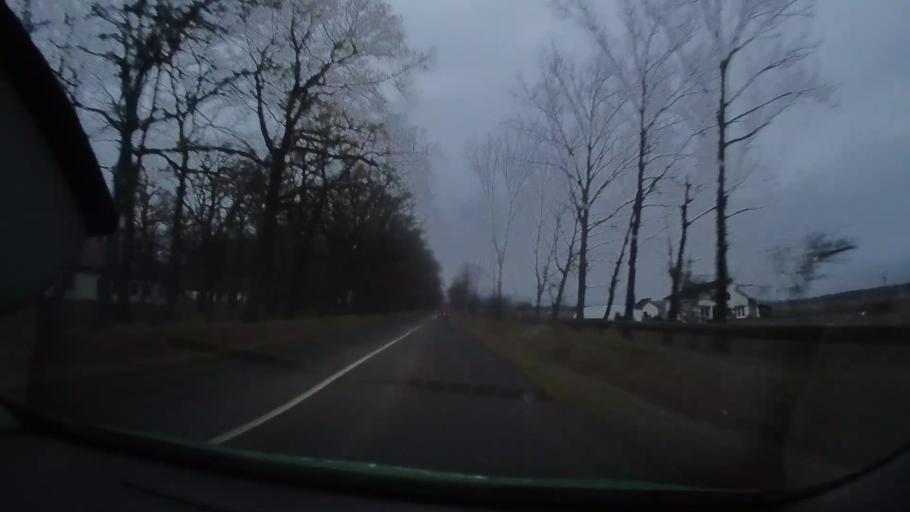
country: RO
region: Mures
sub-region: Comuna Solovastru
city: Solovastru
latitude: 46.7697
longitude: 24.7509
